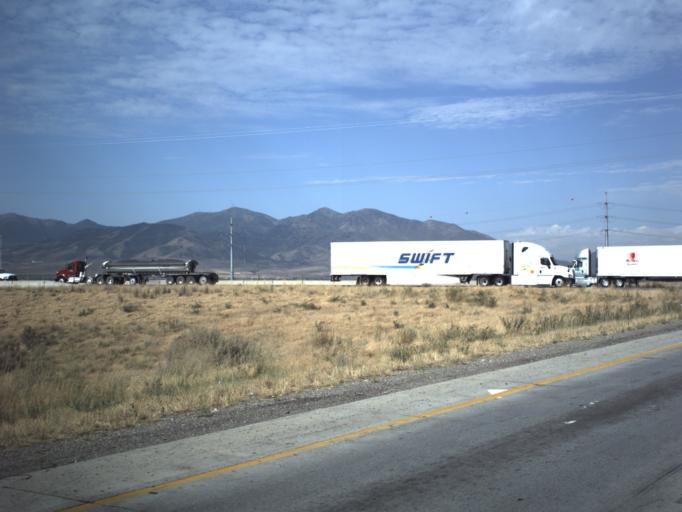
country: US
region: Utah
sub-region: Salt Lake County
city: West Valley City
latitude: 40.7268
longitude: -112.0239
